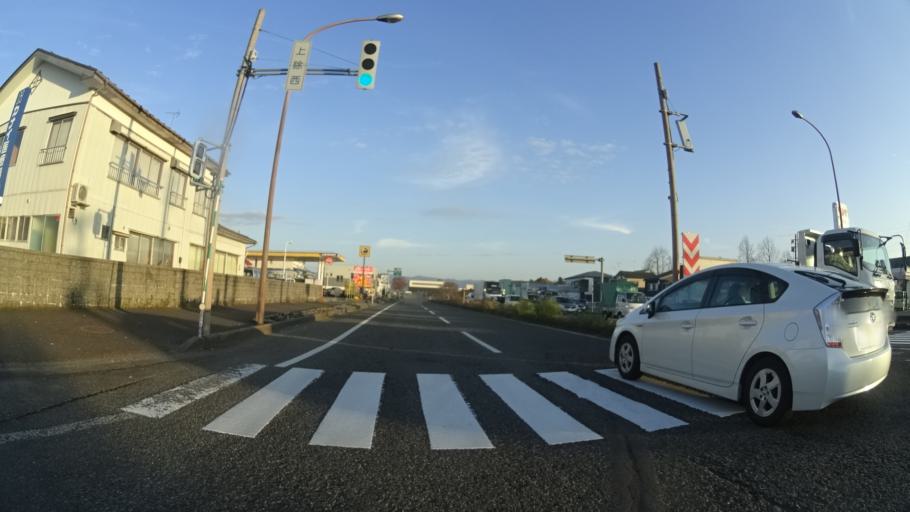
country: JP
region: Niigata
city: Nagaoka
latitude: 37.4463
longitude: 138.7755
